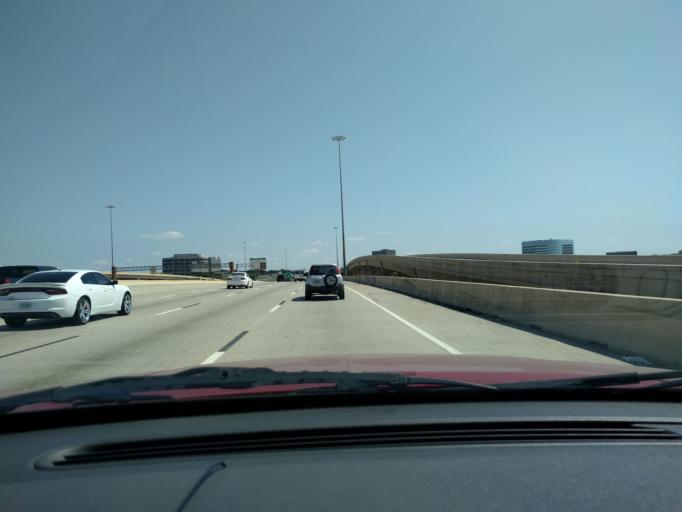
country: US
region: Texas
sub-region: Dallas County
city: Richardson
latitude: 32.9209
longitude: -96.7511
